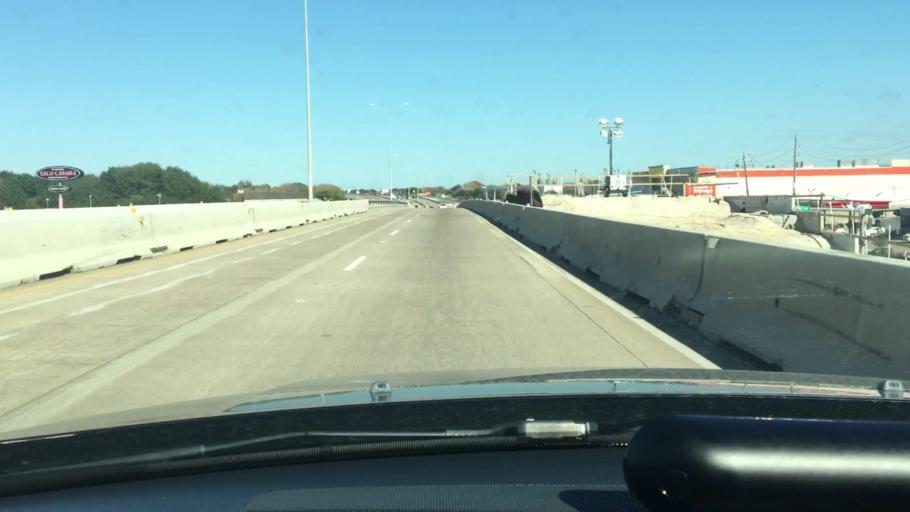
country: US
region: Texas
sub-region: Harris County
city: Deer Park
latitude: 29.6831
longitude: -95.1548
